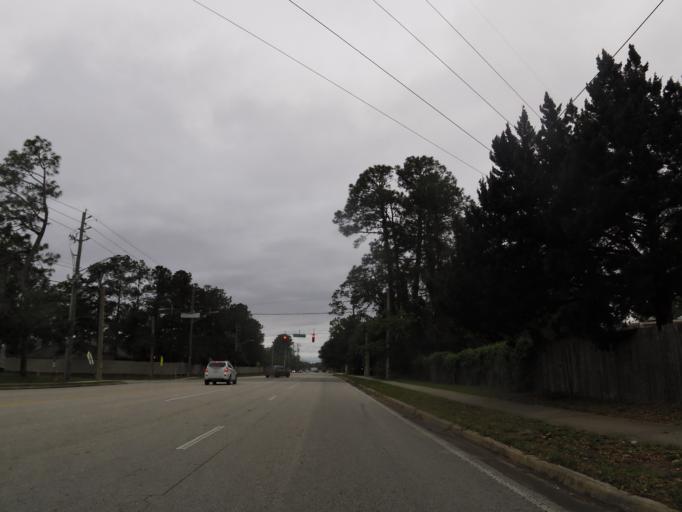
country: US
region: Florida
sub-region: Saint Johns County
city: Fruit Cove
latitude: 30.1959
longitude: -81.6124
